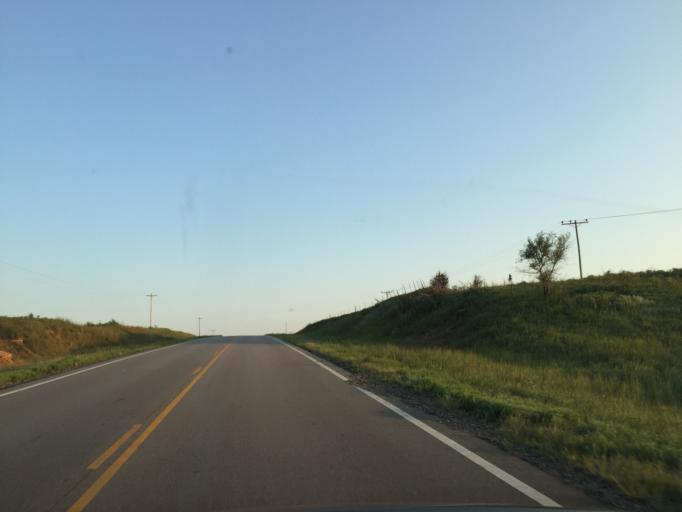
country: US
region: Kansas
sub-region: Ellsworth County
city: Ellsworth
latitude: 38.5751
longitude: -98.2018
